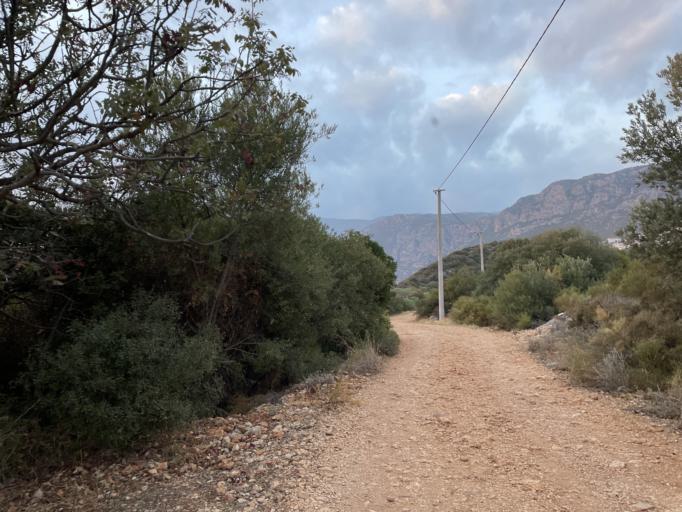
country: TR
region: Antalya
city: Kas
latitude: 36.1843
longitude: 29.6524
